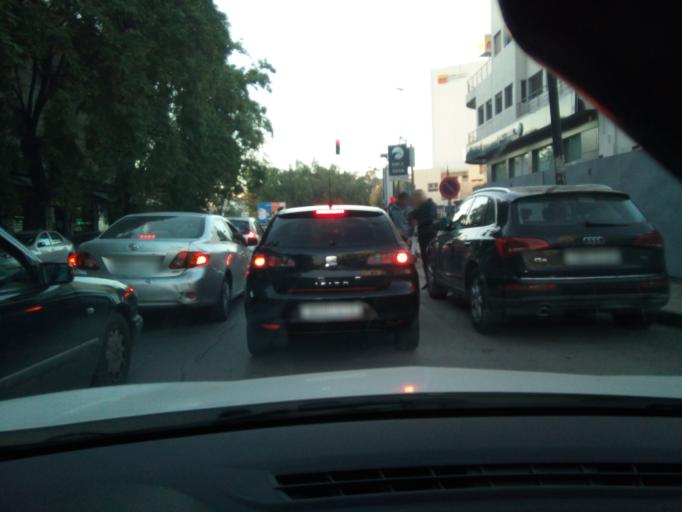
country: MA
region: Fes-Boulemane
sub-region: Fes
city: Fes
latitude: 34.0316
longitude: -4.9940
